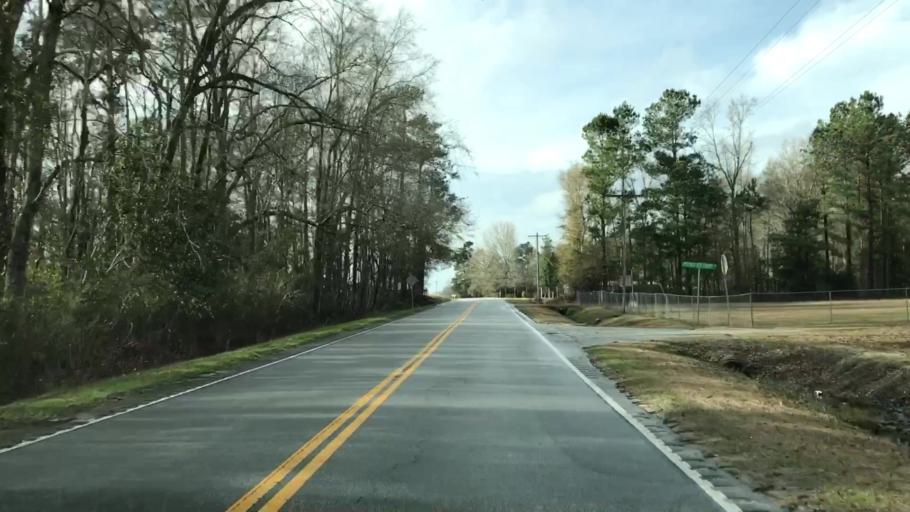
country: US
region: South Carolina
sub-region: Williamsburg County
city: Andrews
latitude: 33.5005
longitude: -79.5157
